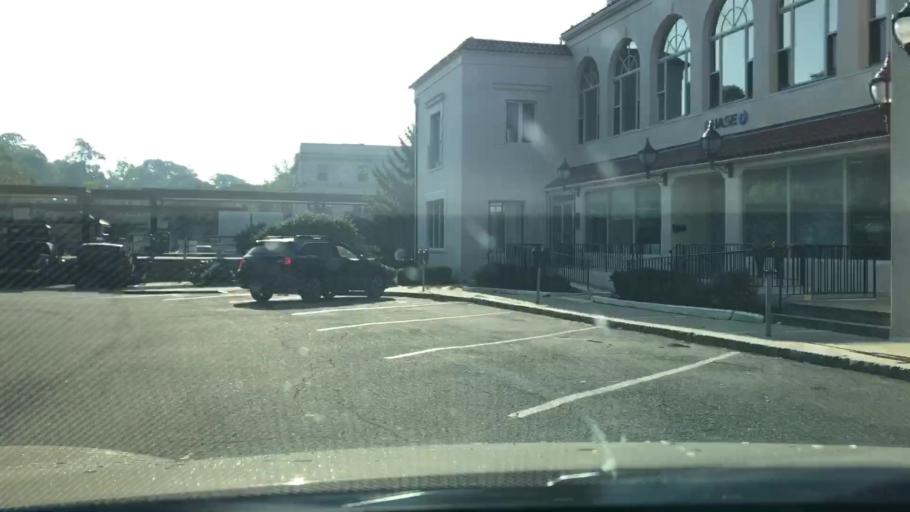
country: US
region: New York
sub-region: Westchester County
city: Bronxville
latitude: 40.9410
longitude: -73.8356
